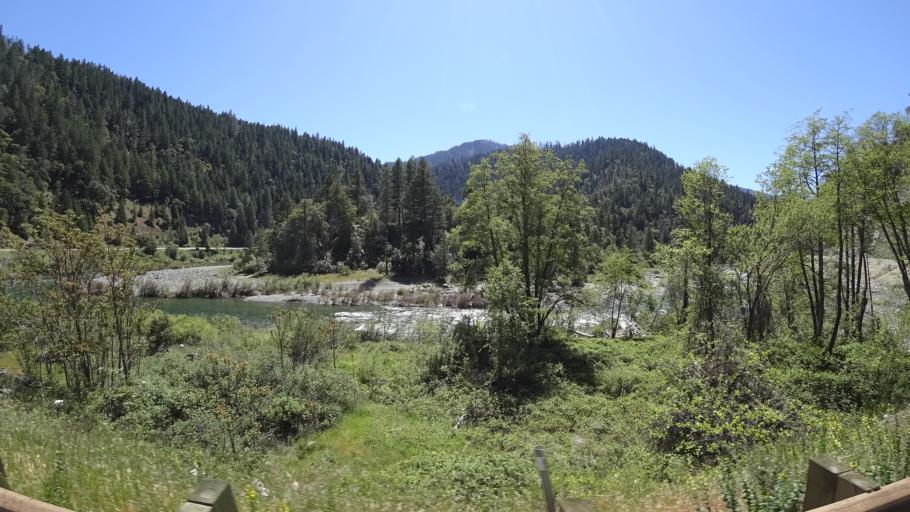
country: US
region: California
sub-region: Trinity County
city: Hayfork
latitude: 40.7799
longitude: -123.3093
